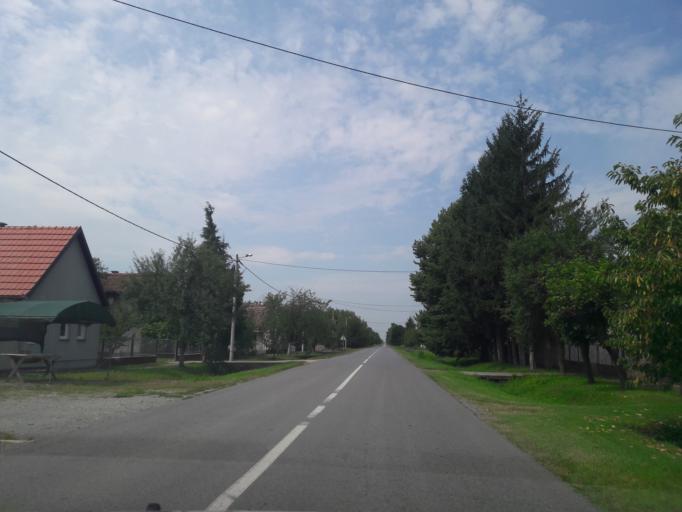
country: HR
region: Osjecko-Baranjska
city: Vuka
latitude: 45.5025
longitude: 18.4484
